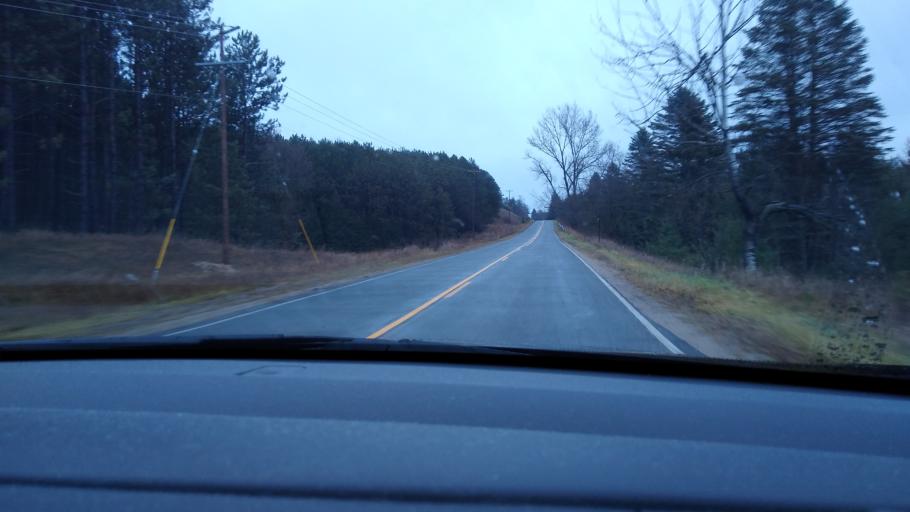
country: US
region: Michigan
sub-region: Wexford County
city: Cadillac
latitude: 44.1650
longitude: -85.3946
